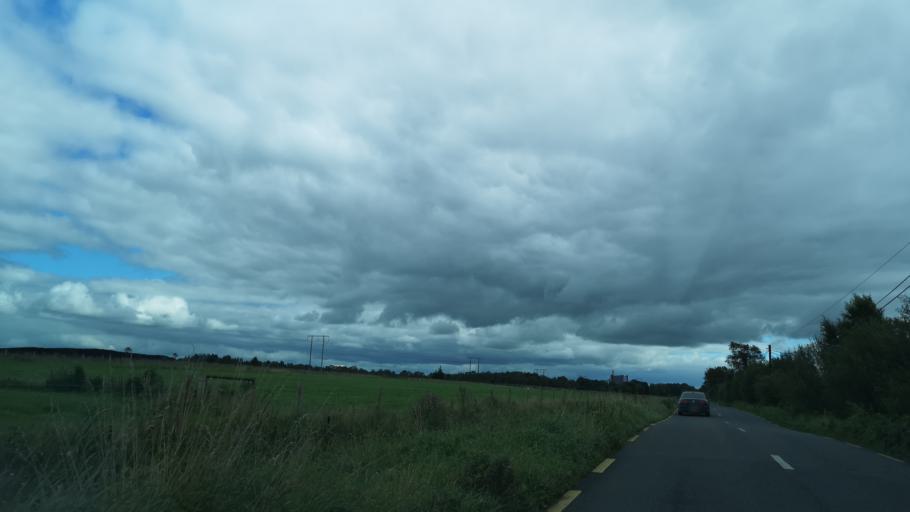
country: IE
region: Leinster
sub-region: Uibh Fhaili
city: Banagher
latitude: 53.2844
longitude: -8.0754
